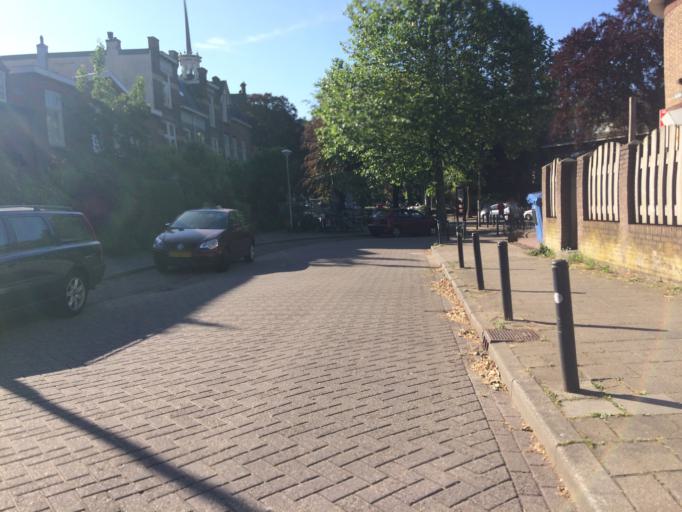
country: NL
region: Gelderland
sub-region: Gemeente Nijmegen
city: Nijmegen
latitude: 51.8349
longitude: 5.8798
